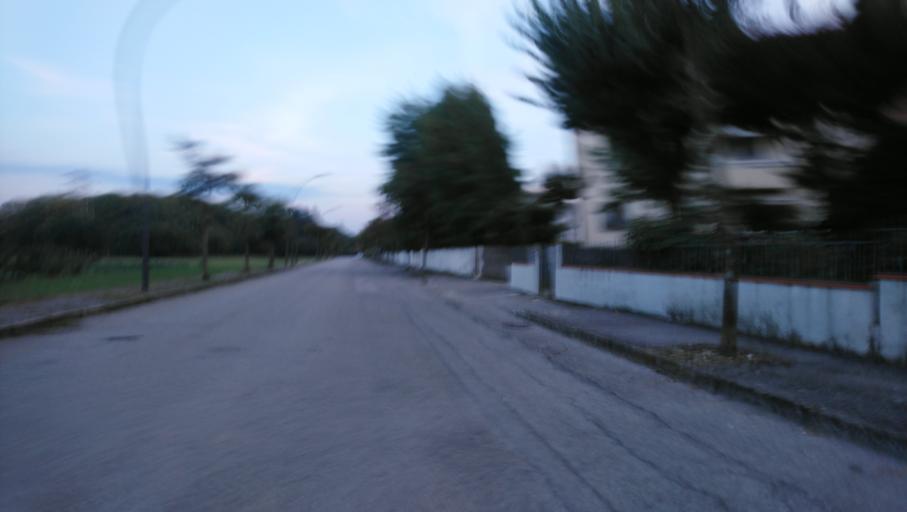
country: IT
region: Veneto
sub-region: Provincia di Treviso
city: Treviso
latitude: 45.6959
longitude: 12.2304
